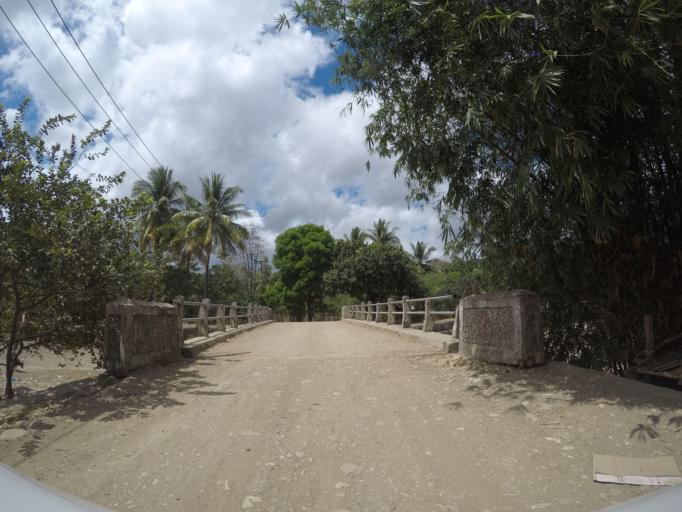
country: TL
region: Lautem
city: Lospalos
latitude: -8.5111
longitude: 126.8326
